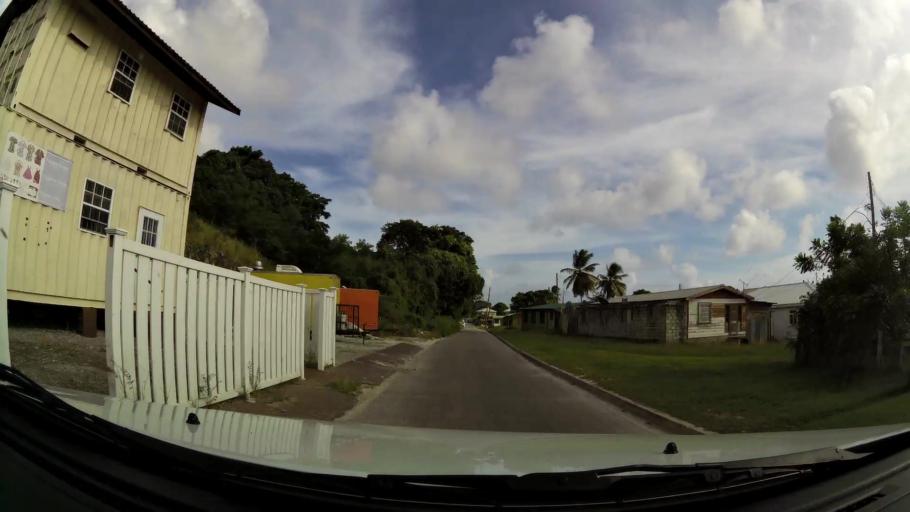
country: BB
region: Saint Michael
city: Bridgetown
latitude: 13.0853
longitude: -59.5810
